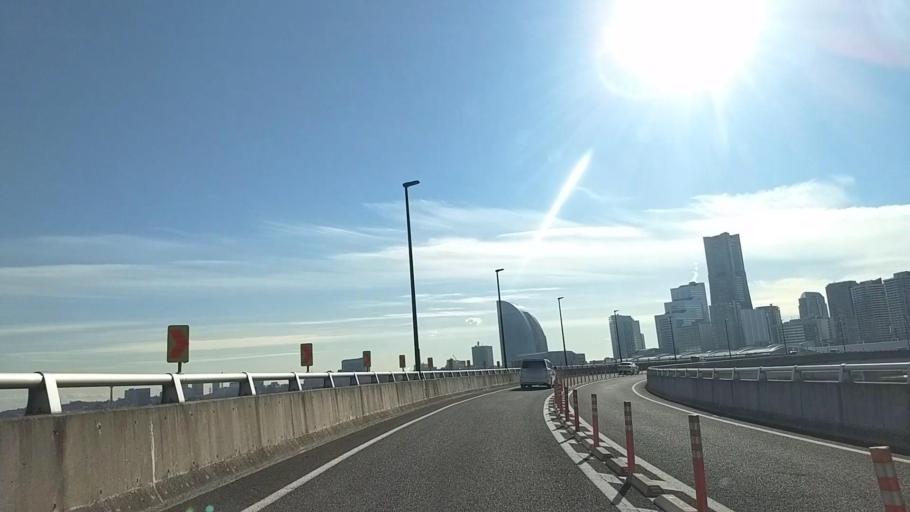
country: JP
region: Kanagawa
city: Yokohama
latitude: 35.4682
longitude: 139.6400
